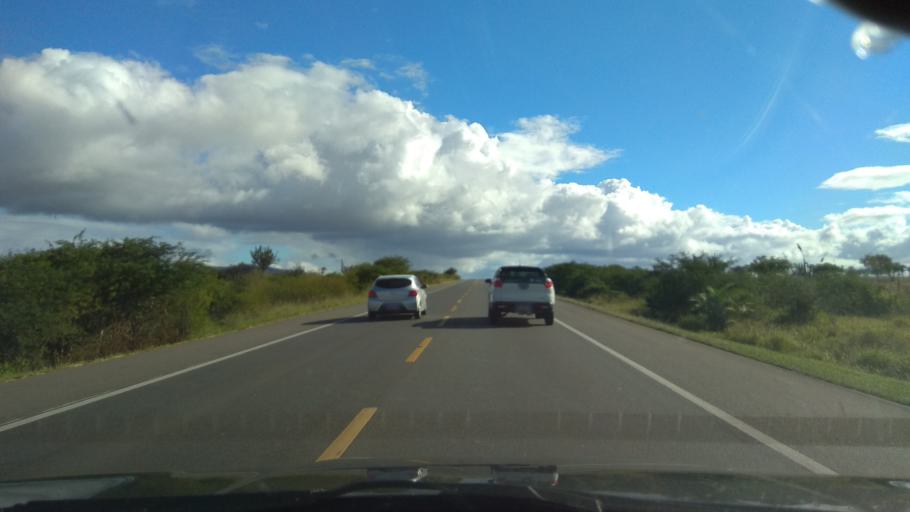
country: BR
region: Bahia
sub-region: Castro Alves
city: Castro Alves
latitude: -12.6727
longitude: -39.6544
